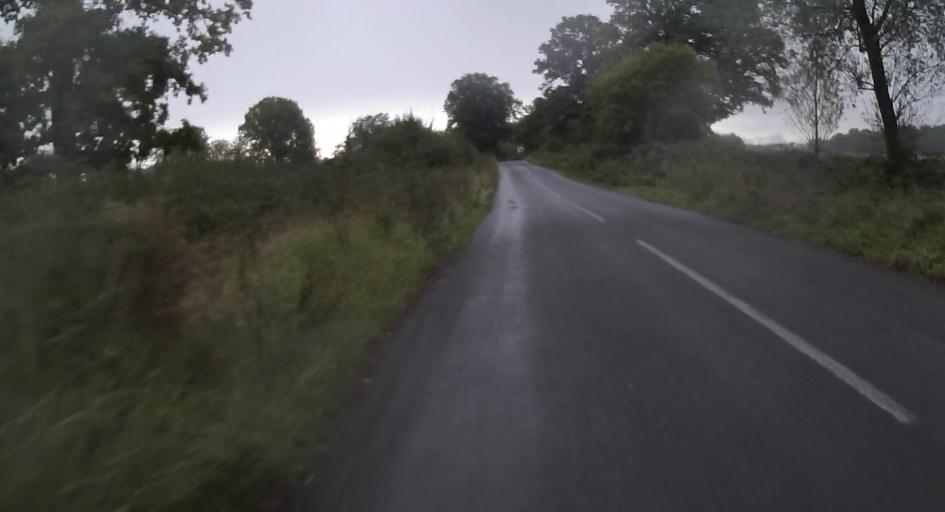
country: GB
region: England
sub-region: Hampshire
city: Tadley
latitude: 51.3119
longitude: -1.1410
